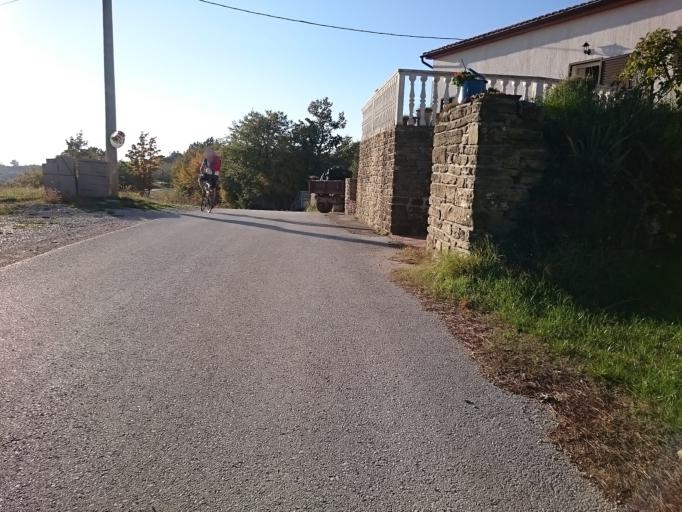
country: HR
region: Istarska
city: Buje
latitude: 45.3848
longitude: 13.7191
